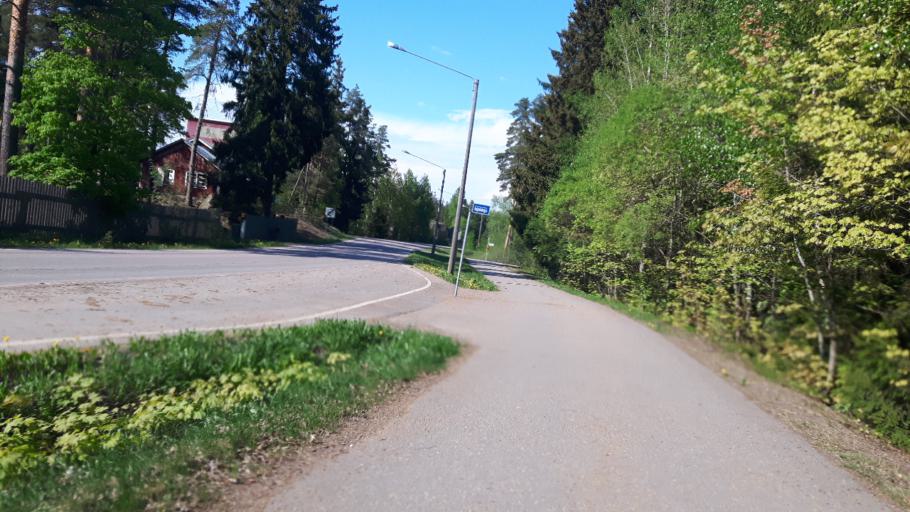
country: FI
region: Kymenlaakso
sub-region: Kotka-Hamina
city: Broby
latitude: 60.4948
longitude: 26.7713
